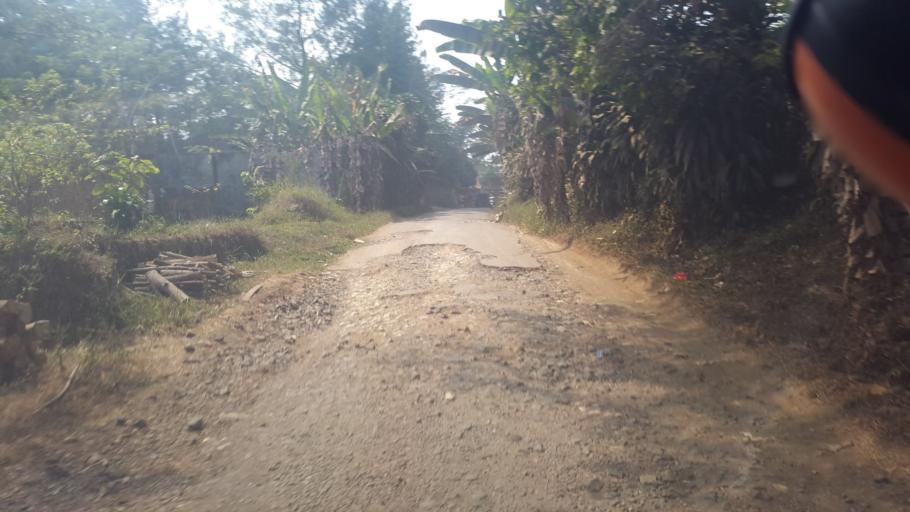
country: ID
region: West Java
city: Pasirlaja
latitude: -7.0547
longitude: 106.8739
